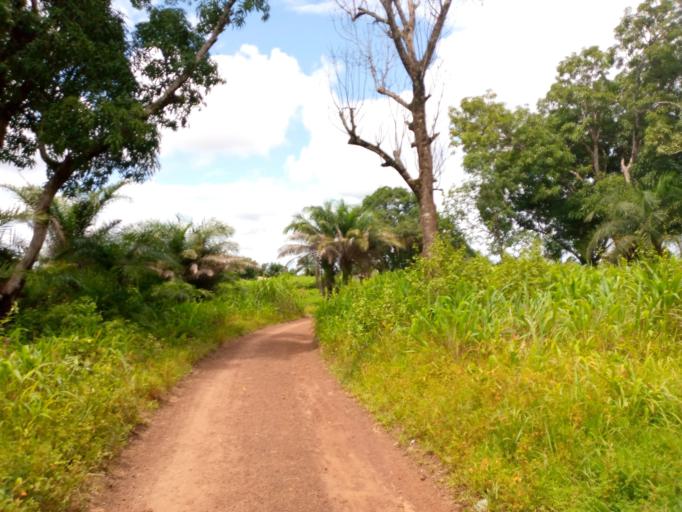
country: SL
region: Northern Province
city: Magburaka
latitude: 8.7241
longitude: -11.9231
